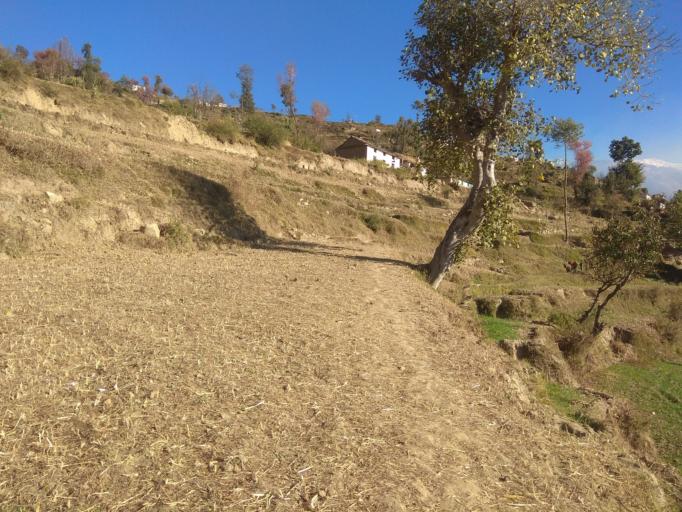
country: NP
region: Far Western
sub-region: Seti Zone
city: Achham
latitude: 29.2529
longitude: 81.6407
